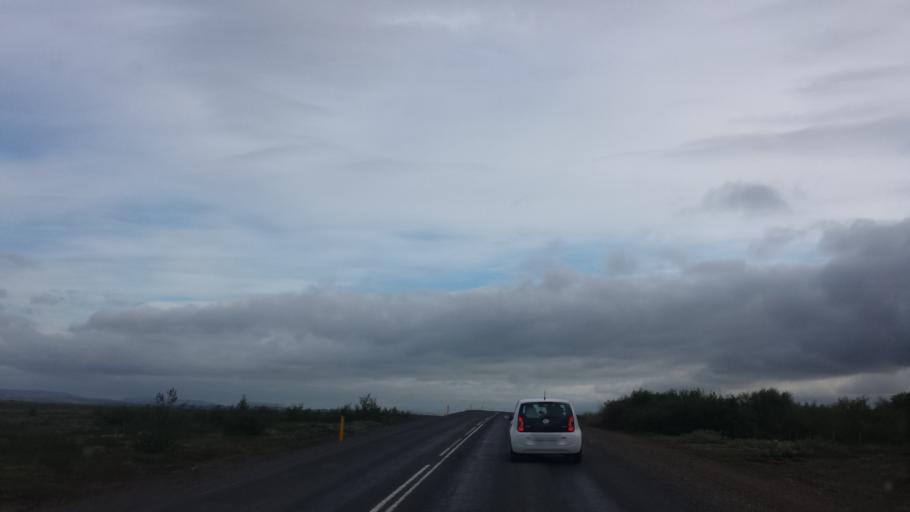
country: IS
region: South
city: Selfoss
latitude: 64.2874
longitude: -20.3394
